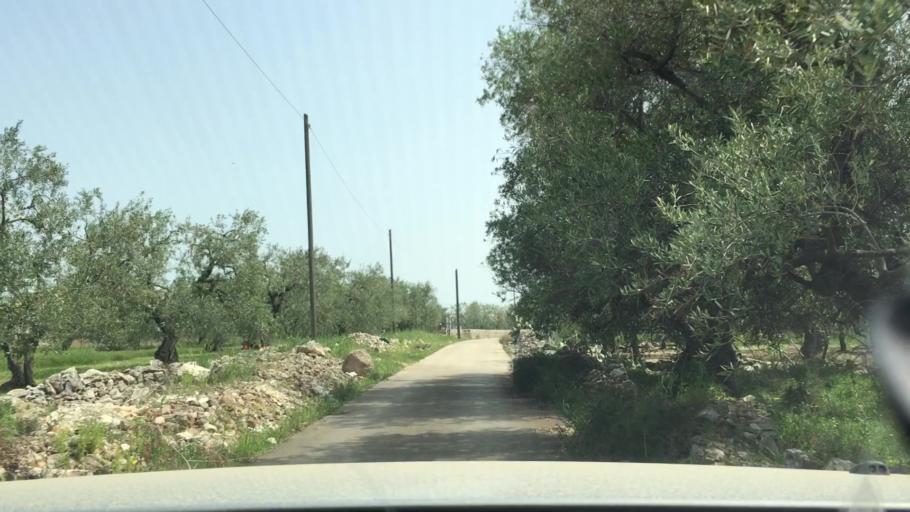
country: IT
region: Apulia
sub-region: Provincia di Barletta - Andria - Trani
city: Capirro
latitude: 41.2556
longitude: 16.4556
